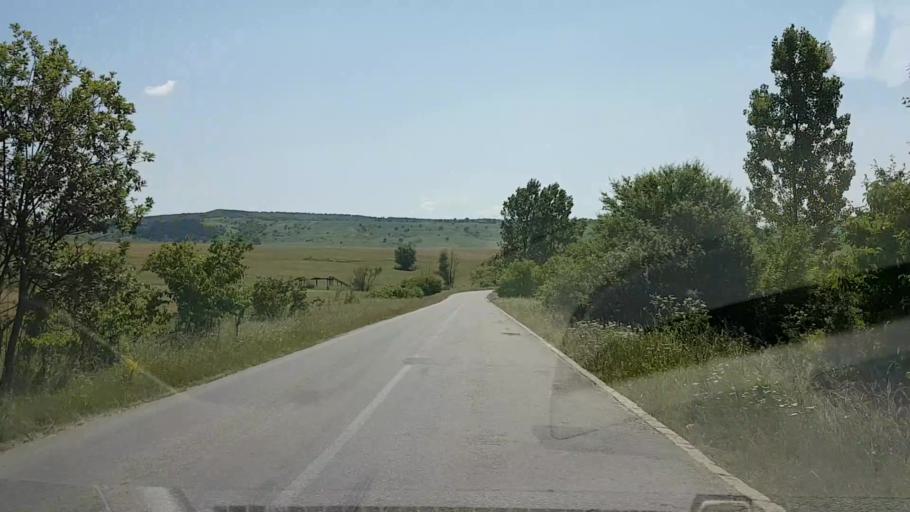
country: RO
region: Brasov
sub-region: Comuna Cincu
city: Cincu
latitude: 45.9331
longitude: 24.7929
